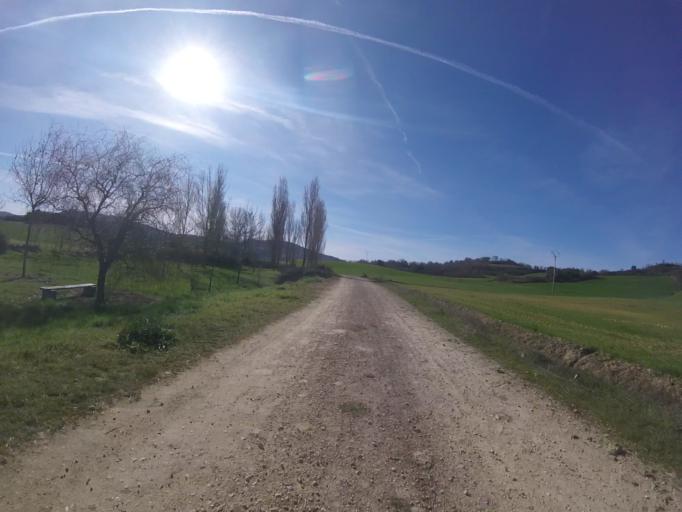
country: ES
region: Navarre
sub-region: Provincia de Navarra
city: Yerri
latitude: 42.6773
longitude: -1.9583
